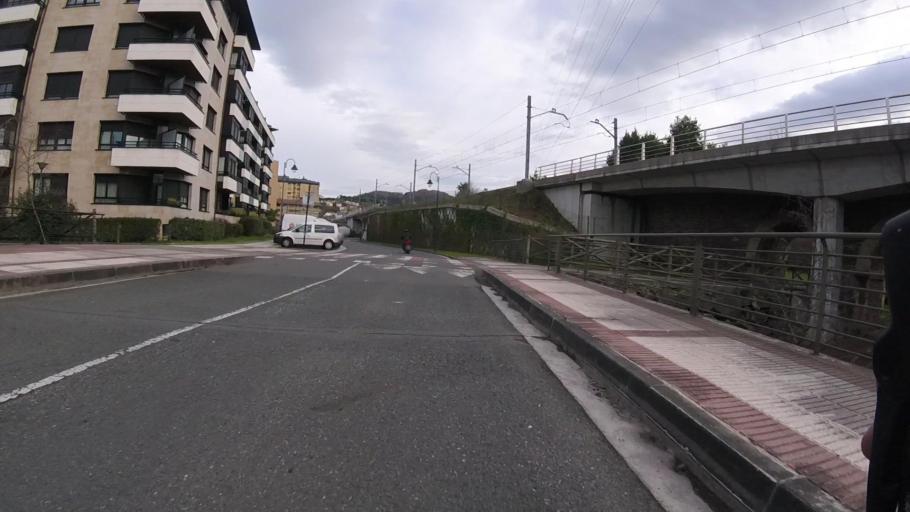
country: ES
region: Basque Country
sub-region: Provincia de Guipuzcoa
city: Lezo
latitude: 43.3085
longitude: -1.8841
